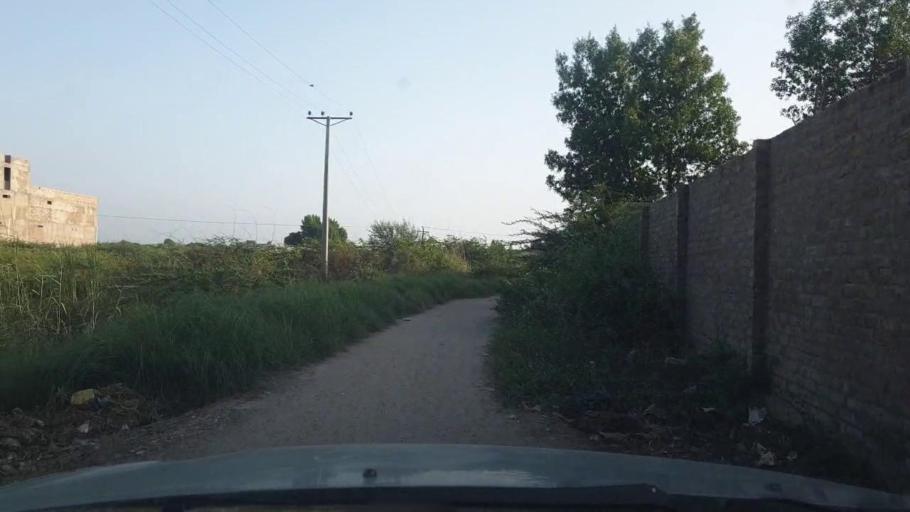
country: PK
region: Sindh
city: Tando Ghulam Ali
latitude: 25.1524
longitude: 68.9599
